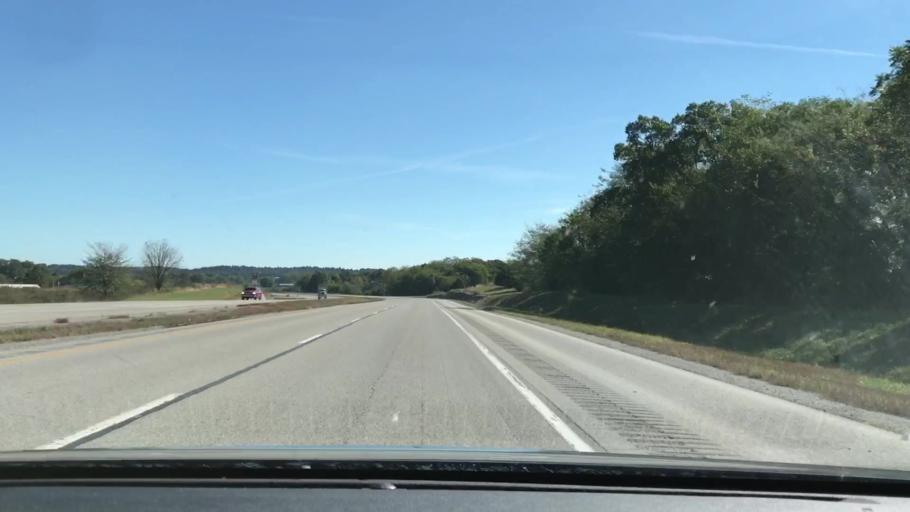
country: US
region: Kentucky
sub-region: Todd County
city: Elkton
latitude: 36.8211
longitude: -87.1748
